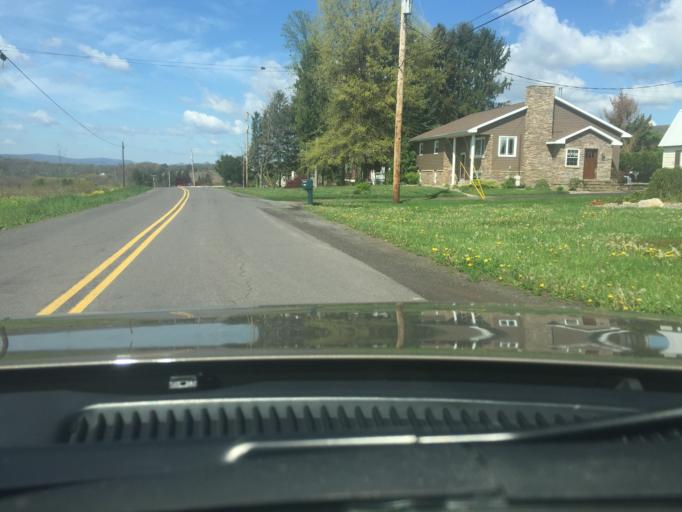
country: US
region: Pennsylvania
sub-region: Luzerne County
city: Conyngham
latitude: 41.0282
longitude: -76.0479
